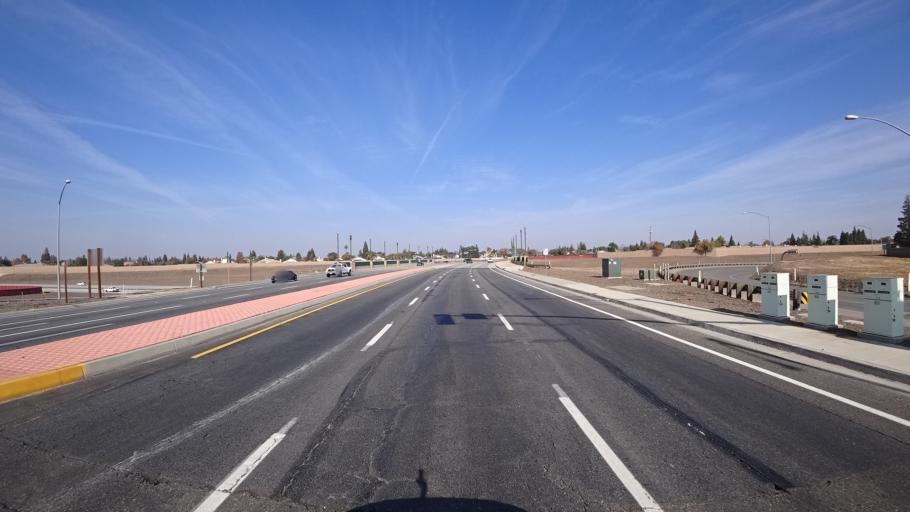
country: US
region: California
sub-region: Kern County
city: Greenacres
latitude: 35.3608
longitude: -119.1160
